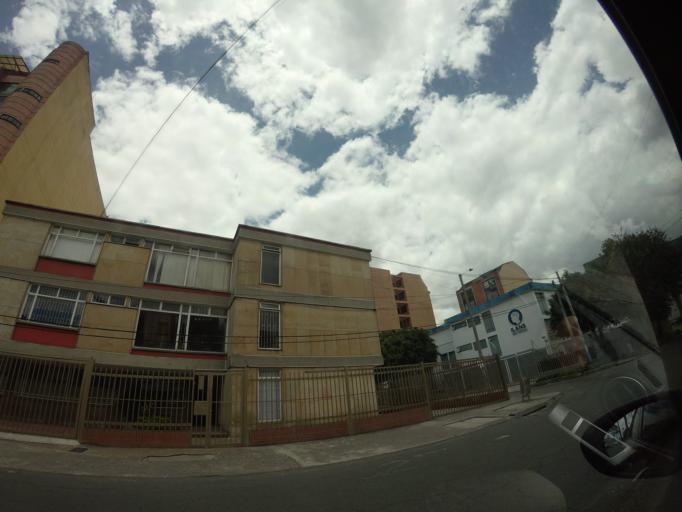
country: CO
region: Bogota D.C.
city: Barrio San Luis
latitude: 4.6691
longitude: -74.0592
